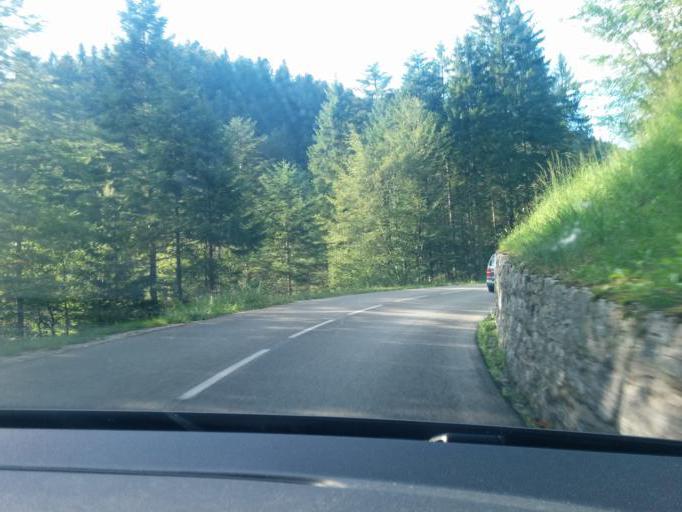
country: FR
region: Franche-Comte
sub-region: Departement du Jura
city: Saint-Lupicin
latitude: 46.4474
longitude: 5.8060
